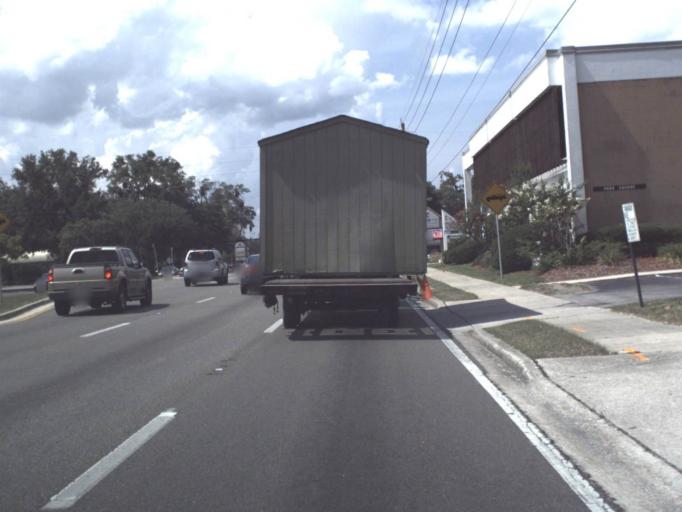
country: US
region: Florida
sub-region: Clay County
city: Orange Park
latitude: 30.1636
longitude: -81.7009
